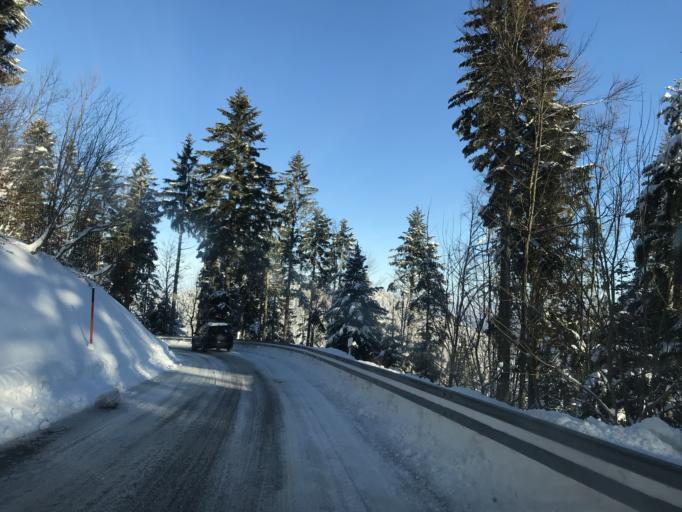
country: DE
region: Baden-Wuerttemberg
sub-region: Freiburg Region
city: Muenstertal/Schwarzwald
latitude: 47.8078
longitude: 7.7850
